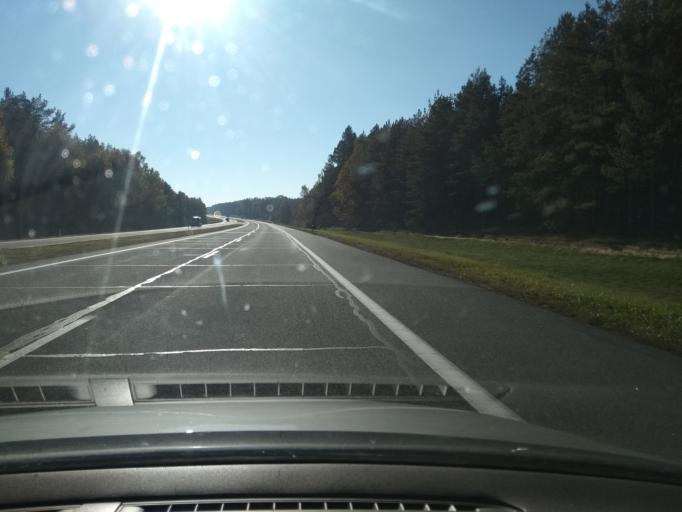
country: BY
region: Brest
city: Baranovichi
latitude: 53.0247
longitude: 25.7933
